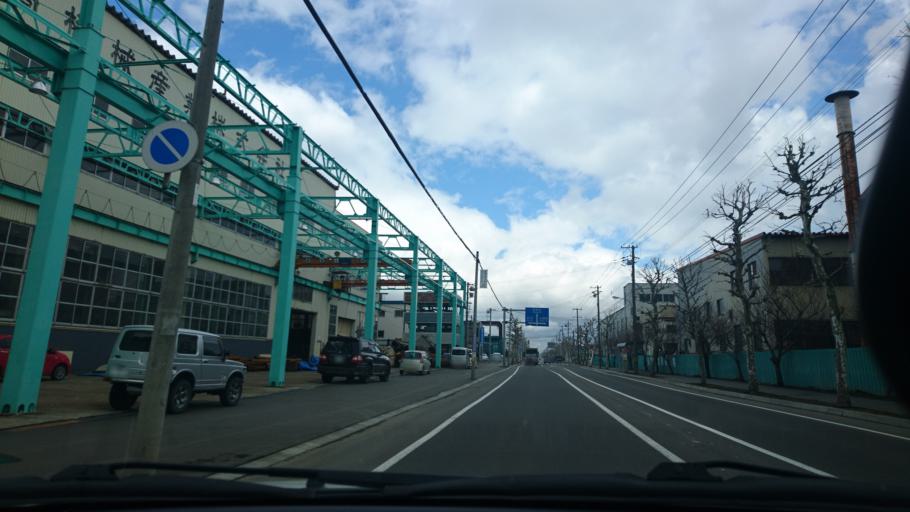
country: JP
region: Hokkaido
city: Sapporo
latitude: 43.1041
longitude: 141.2838
